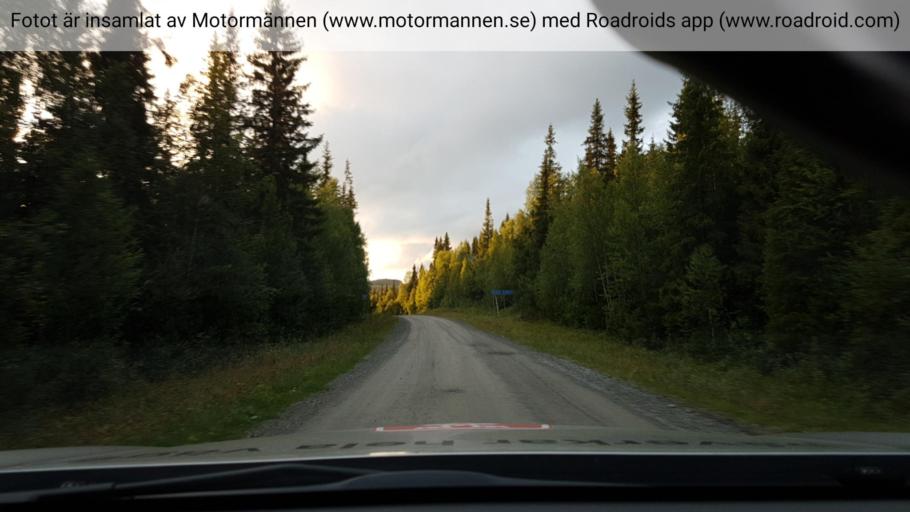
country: SE
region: Vaesterbotten
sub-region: Vilhelmina Kommun
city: Sjoberg
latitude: 65.5540
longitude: 15.4099
